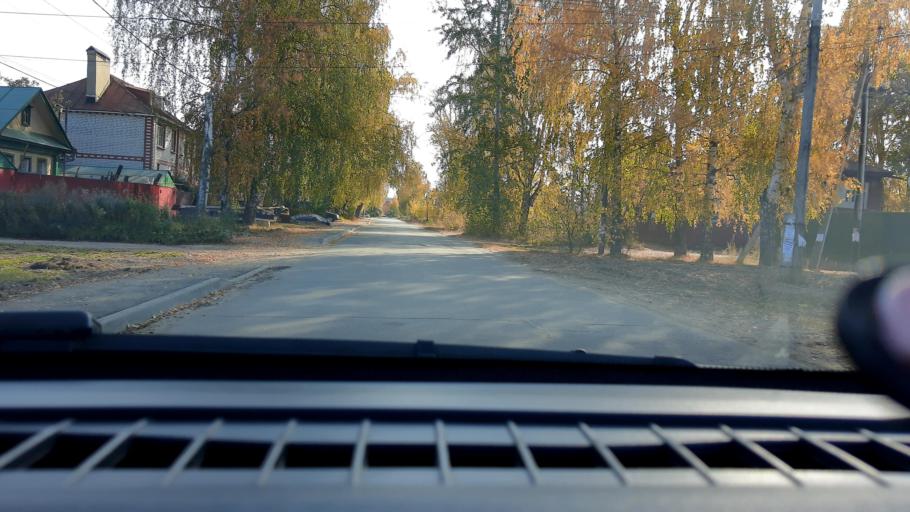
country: RU
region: Nizjnij Novgorod
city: Gorbatovka
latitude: 56.2090
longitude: 43.7592
